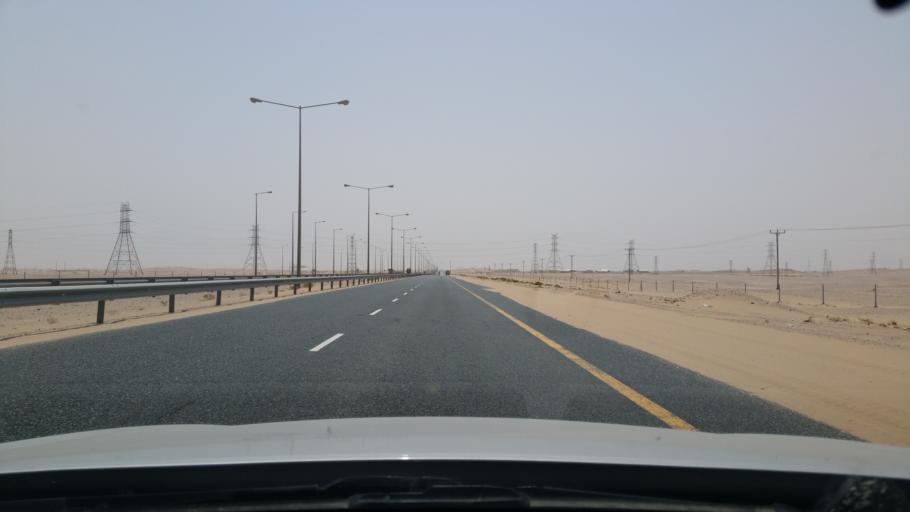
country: QA
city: Umm Bab
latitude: 24.9639
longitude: 50.9618
